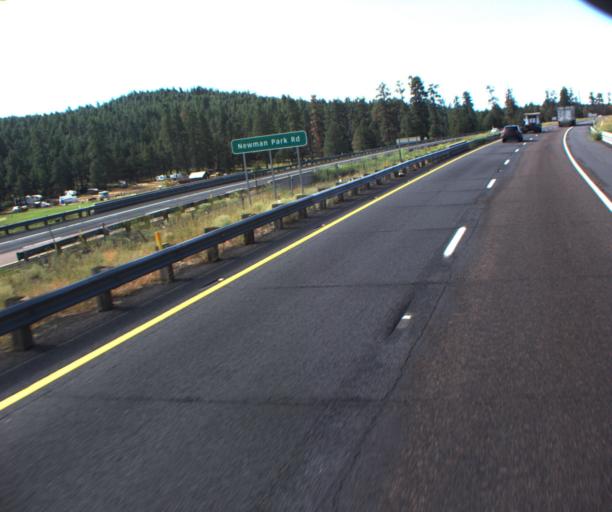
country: US
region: Arizona
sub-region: Coconino County
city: Mountainaire
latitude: 35.0190
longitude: -111.6850
